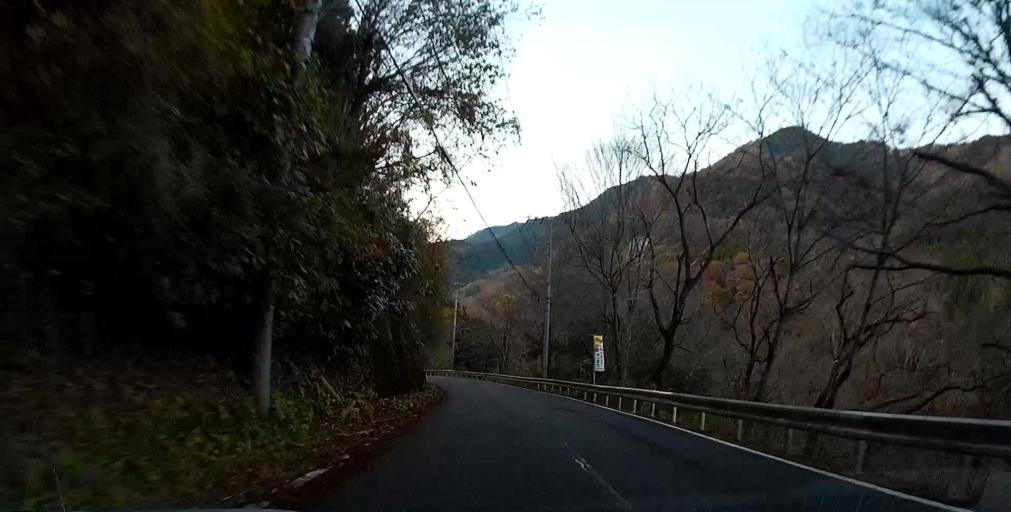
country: JP
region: Yamanashi
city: Uenohara
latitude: 35.5662
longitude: 139.2084
